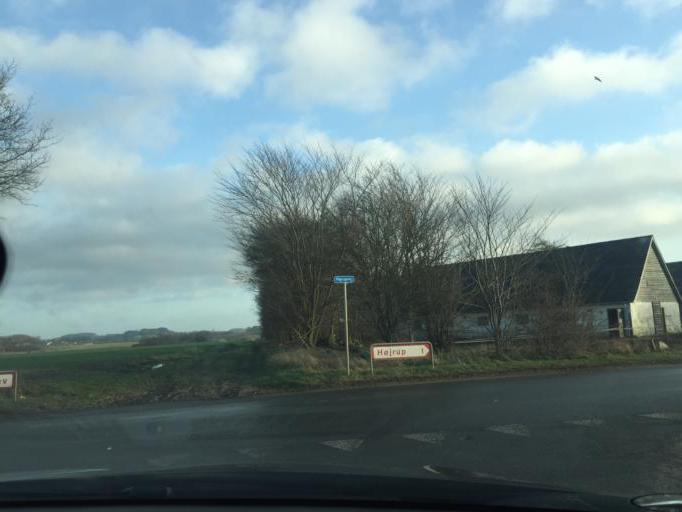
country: DK
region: South Denmark
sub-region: Odense Kommune
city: Bellinge
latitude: 55.2005
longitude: 10.3397
